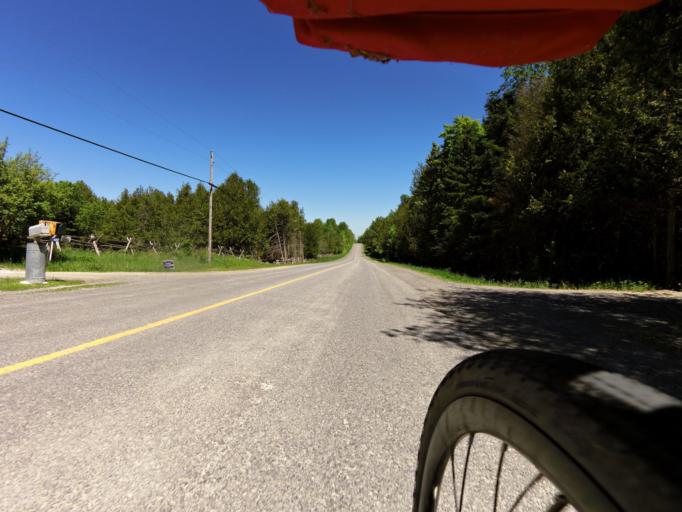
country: CA
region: Ontario
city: Carleton Place
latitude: 45.1643
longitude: -76.4254
